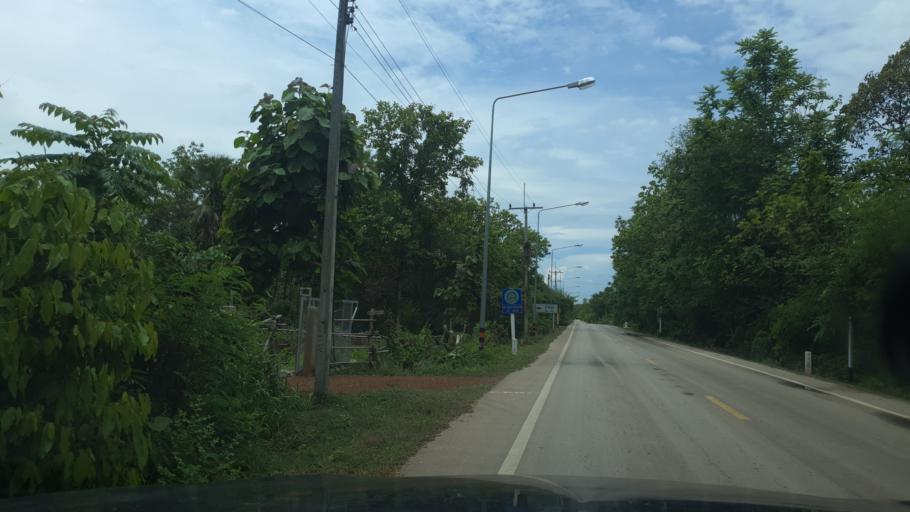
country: TH
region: Lampang
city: Ko Kha
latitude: 18.2584
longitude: 99.3710
